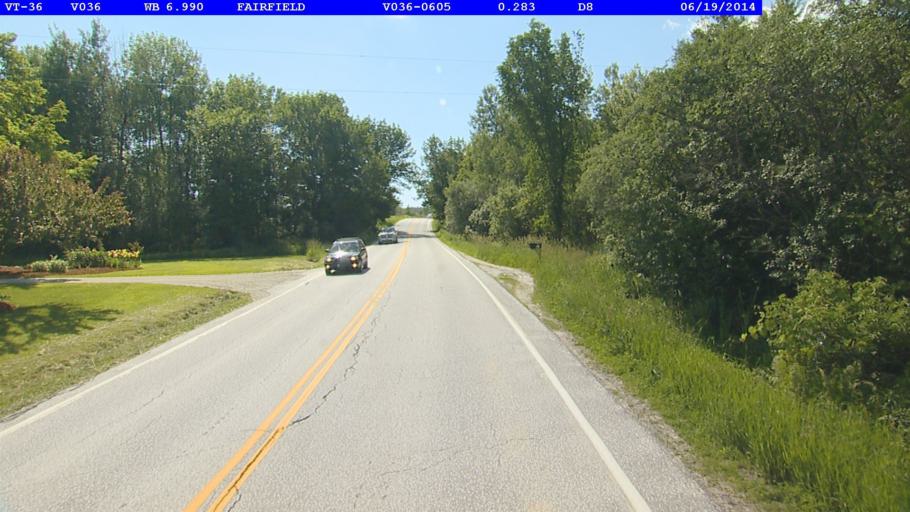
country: US
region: Vermont
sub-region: Franklin County
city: Saint Albans
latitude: 44.7899
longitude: -73.0262
